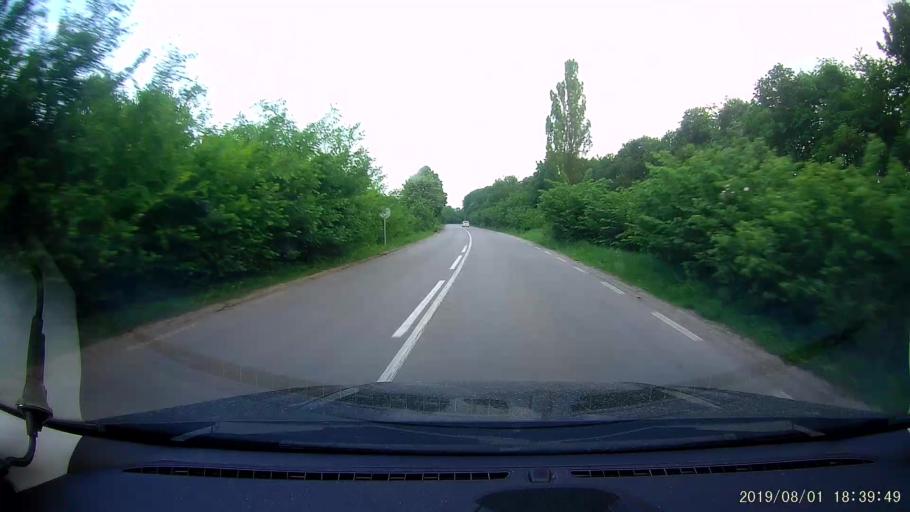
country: BG
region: Shumen
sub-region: Obshtina Khitrino
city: Gara Khitrino
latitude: 43.3779
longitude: 26.9184
